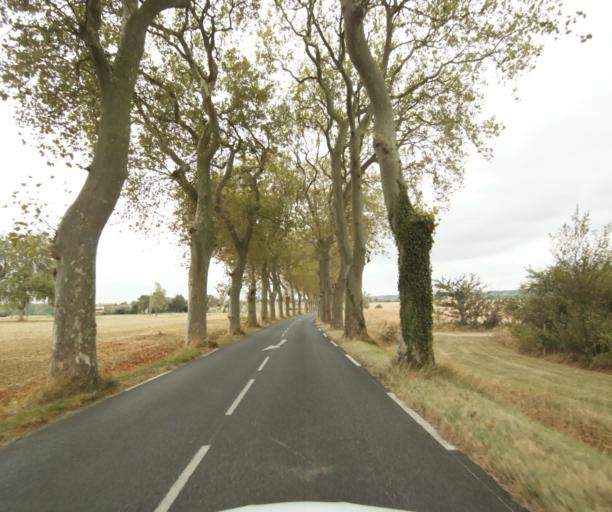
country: FR
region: Midi-Pyrenees
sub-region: Departement de la Haute-Garonne
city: Villefranche-de-Lauragais
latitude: 43.4097
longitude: 1.7338
